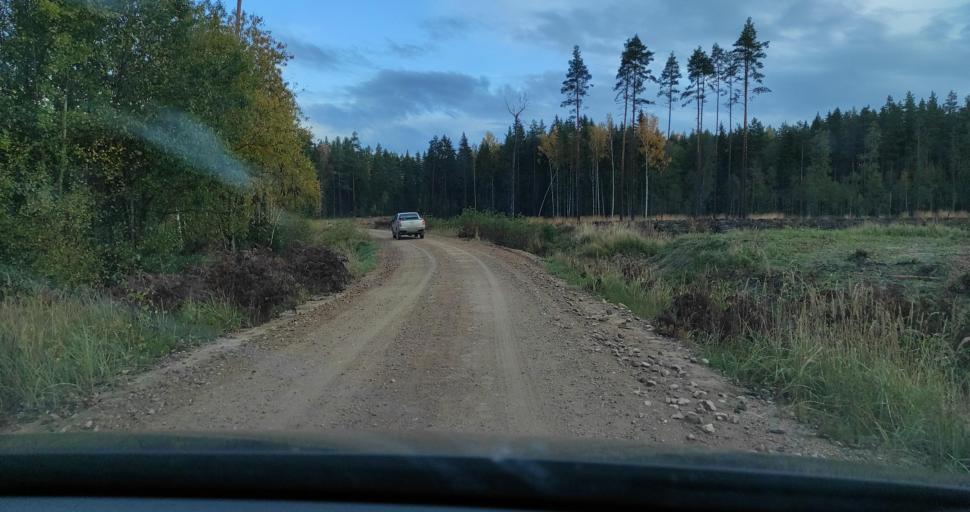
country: LV
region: Kuldigas Rajons
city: Kuldiga
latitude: 57.0362
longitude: 22.0648
